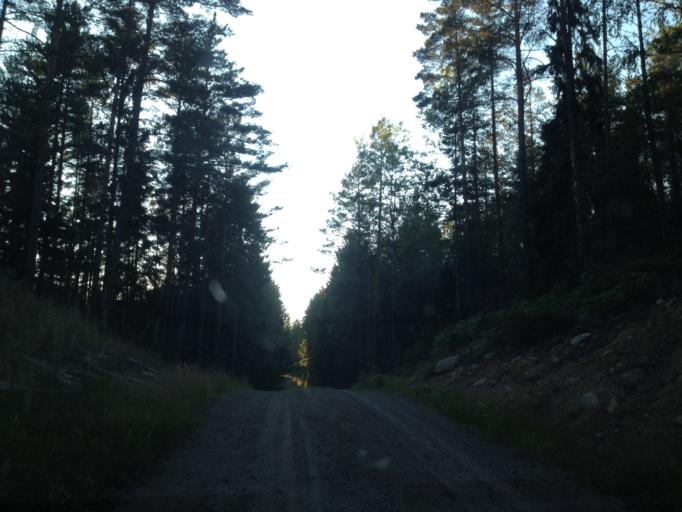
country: SE
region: Kalmar
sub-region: Vasterviks Kommun
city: Overum
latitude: 57.9978
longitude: 16.1355
